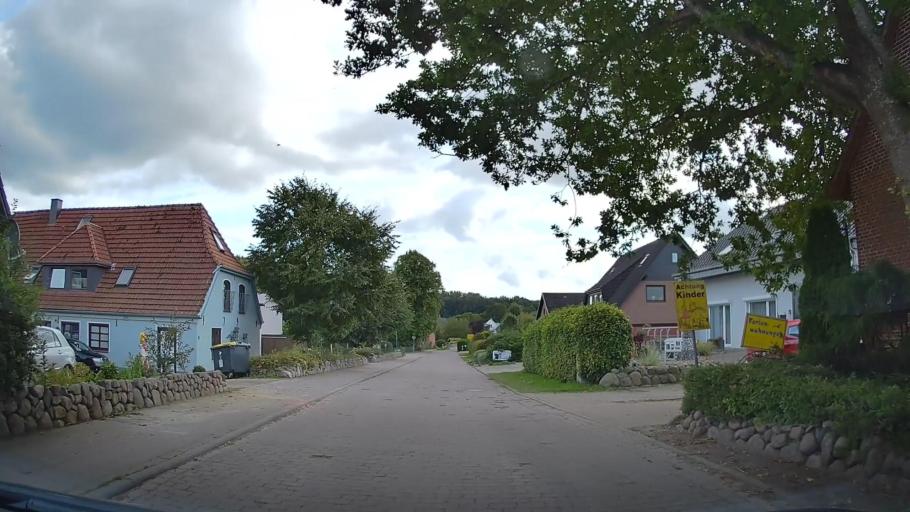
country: DE
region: Schleswig-Holstein
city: Steinberg
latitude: 54.7784
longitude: 9.7996
